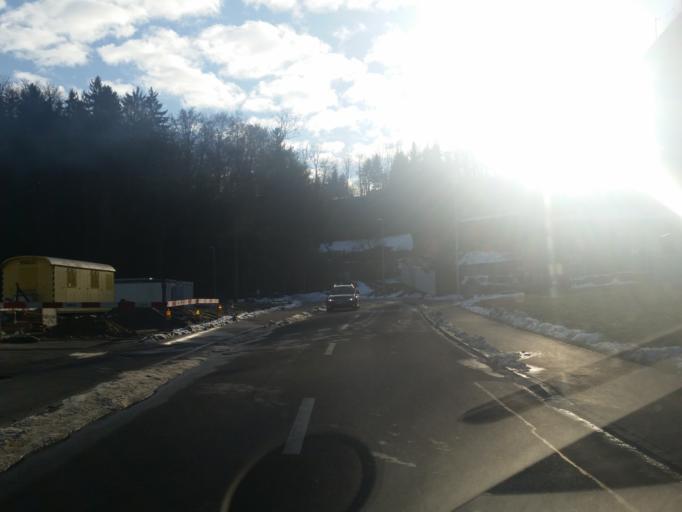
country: CH
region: Zurich
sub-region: Bezirk Dietikon
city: Dietikon / Oberdorf
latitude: 47.3871
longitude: 8.3924
